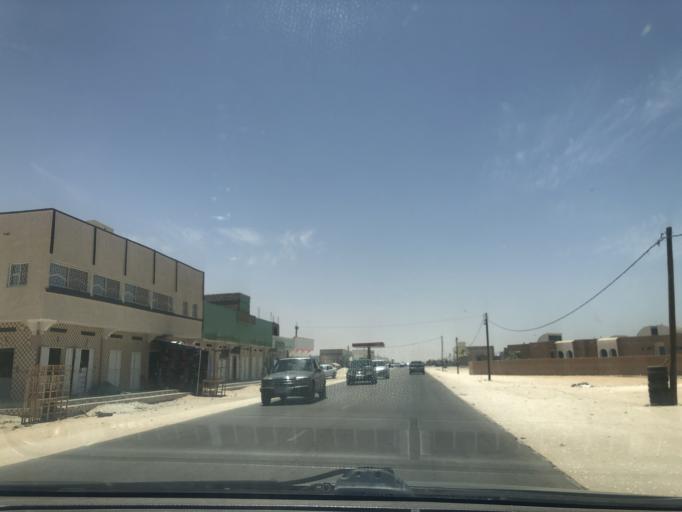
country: MR
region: Nouakchott
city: Nouakchott
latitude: 18.0160
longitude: -15.9589
